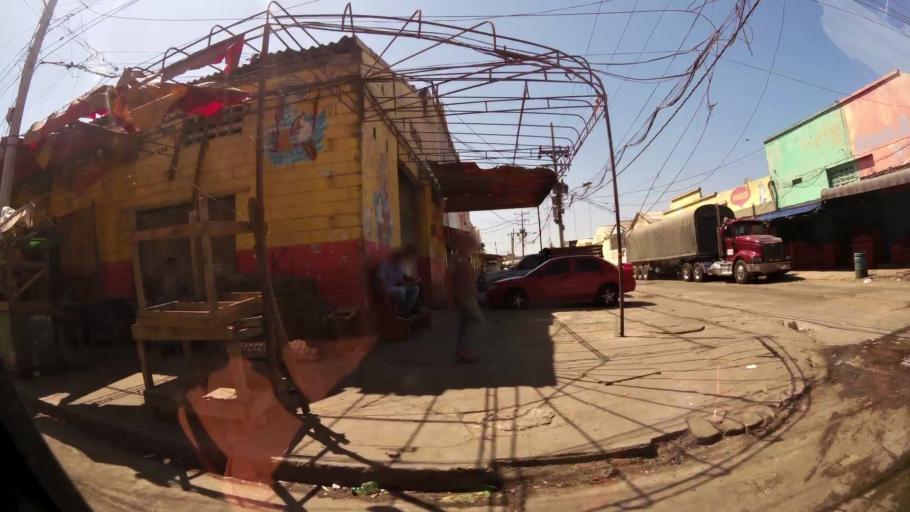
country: CO
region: Atlantico
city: Barranquilla
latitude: 10.9801
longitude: -74.7723
